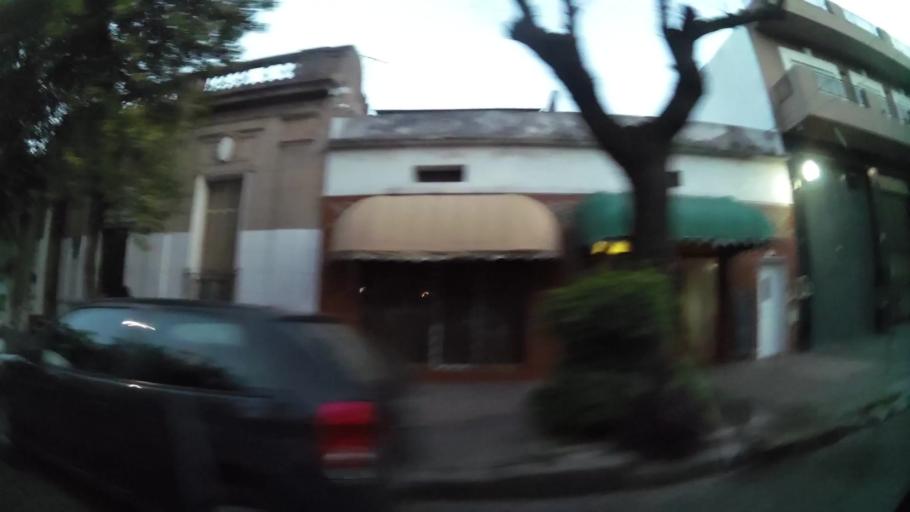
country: AR
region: Buenos Aires F.D.
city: Villa Lugano
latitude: -34.6808
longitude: -58.4759
